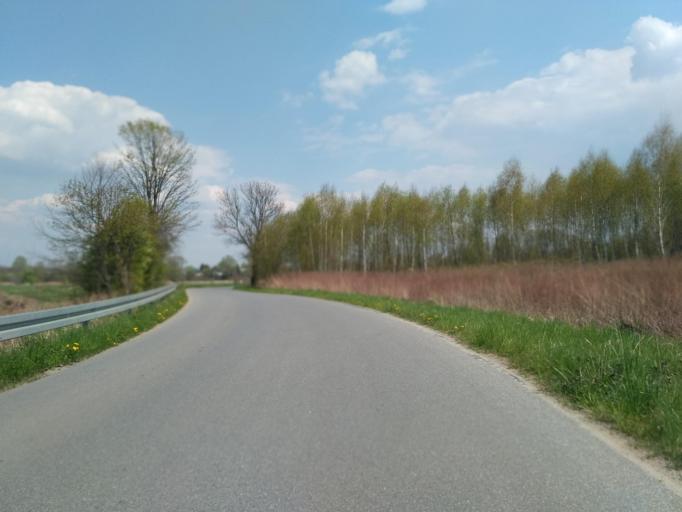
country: PL
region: Subcarpathian Voivodeship
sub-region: Powiat jasielski
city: Tarnowiec
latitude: 49.7370
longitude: 21.5257
